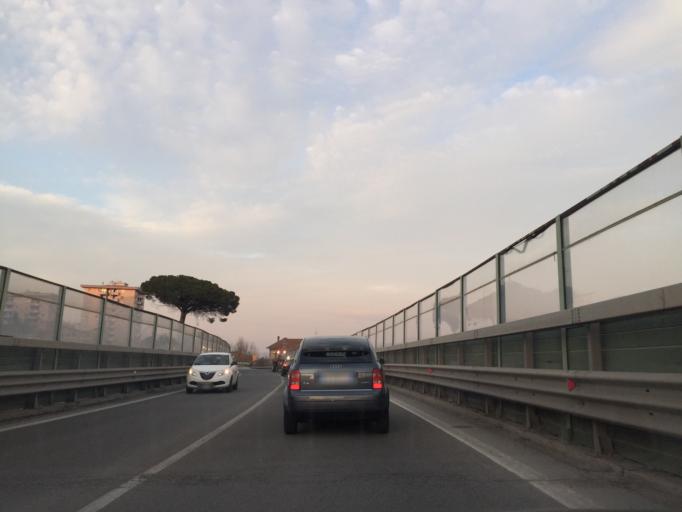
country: IT
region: Molise
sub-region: Provincia di Campobasso
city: Campobasso
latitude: 41.5574
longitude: 14.6754
